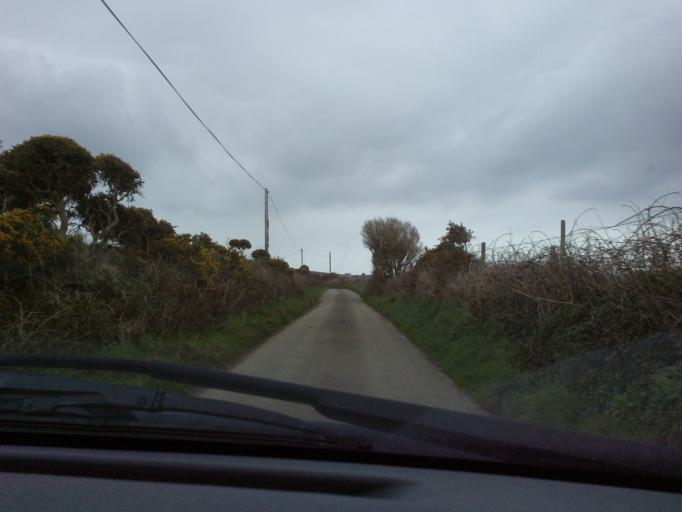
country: GB
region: England
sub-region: Cornwall
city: Saint Just
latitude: 50.1075
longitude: -5.6706
